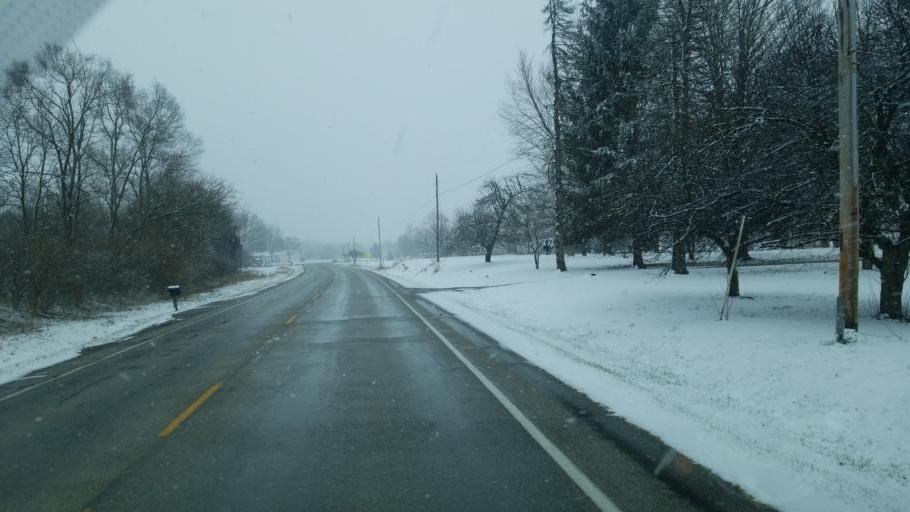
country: US
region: Indiana
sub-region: Wayne County
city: Richmond
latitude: 39.9017
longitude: -84.9476
